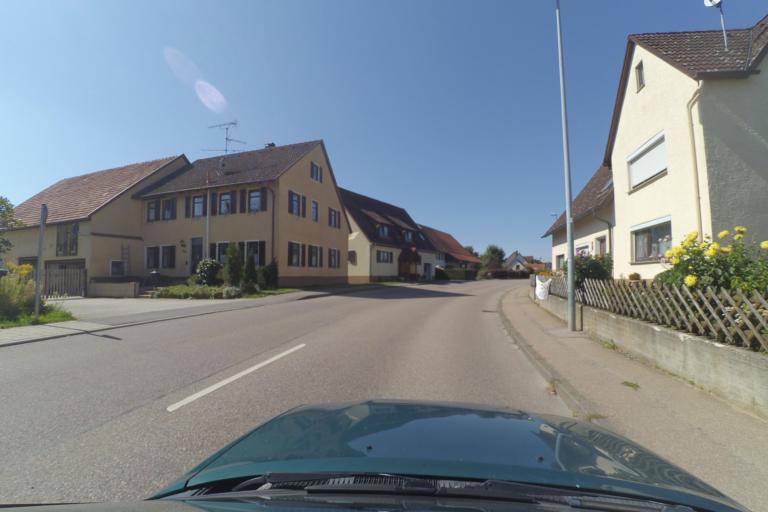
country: DE
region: Baden-Wuerttemberg
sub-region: Regierungsbezirk Stuttgart
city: Steinheim am Albuch
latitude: 48.7288
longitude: 10.0690
